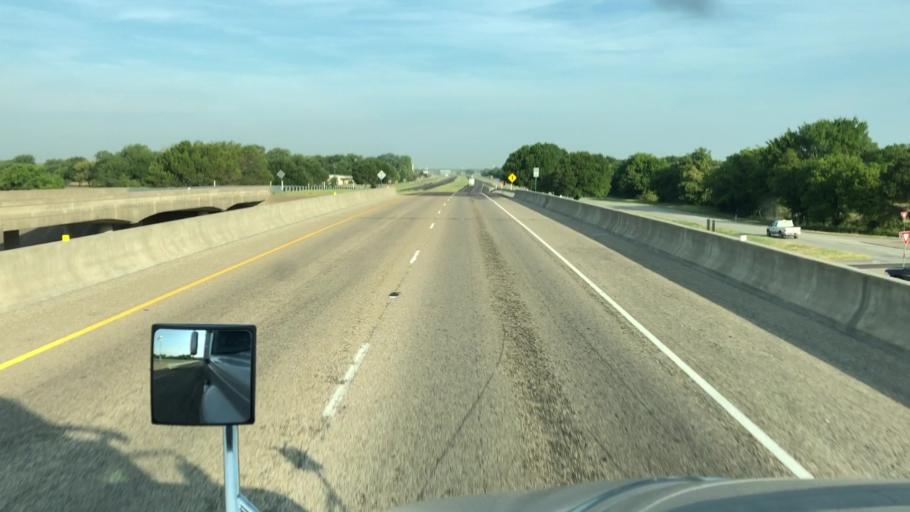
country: US
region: Texas
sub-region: McLennan County
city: Bellmead
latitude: 31.5471
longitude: -97.0692
